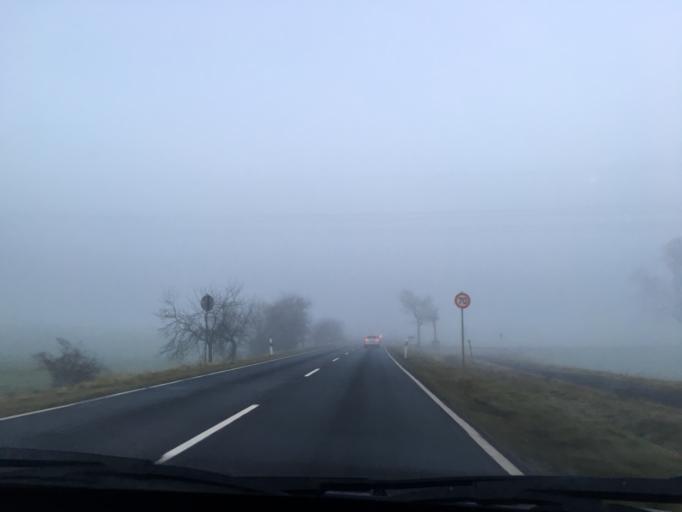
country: DE
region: Hesse
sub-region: Regierungsbezirk Kassel
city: Petersberg
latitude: 50.5648
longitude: 9.7511
